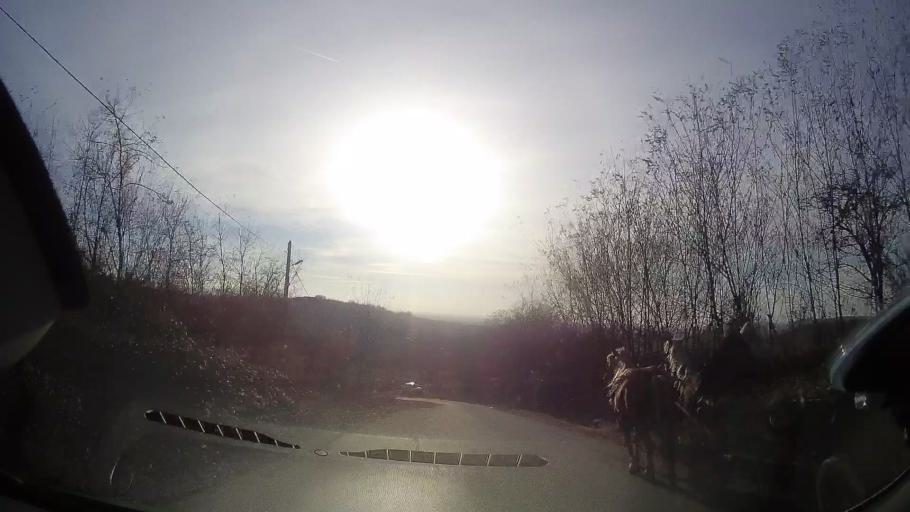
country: RO
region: Bihor
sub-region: Comuna Sarbi
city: Burzuc
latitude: 47.1119
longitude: 22.1780
